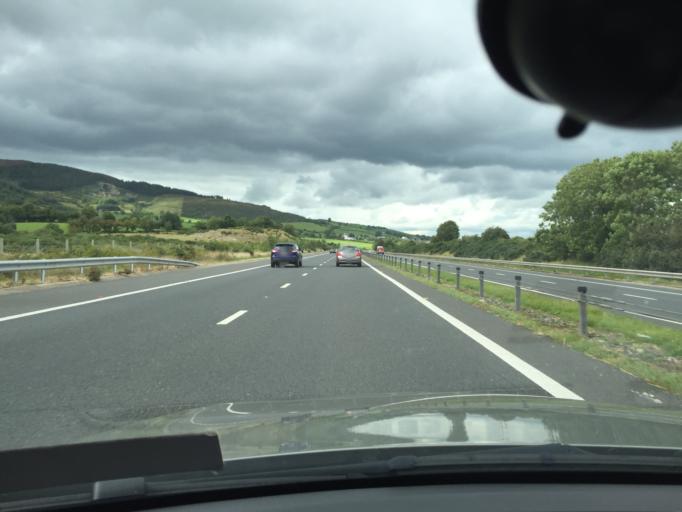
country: GB
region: Northern Ireland
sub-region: Newry and Mourne District
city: Newry
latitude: 54.1564
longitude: -6.3524
